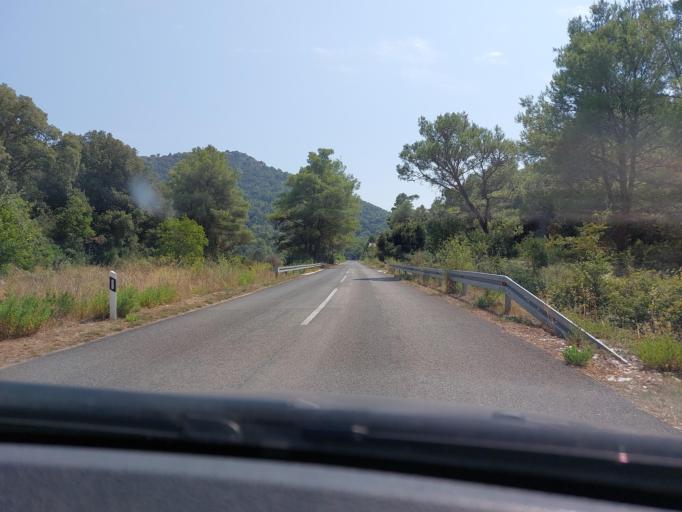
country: HR
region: Dubrovacko-Neretvanska
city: Smokvica
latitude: 42.7519
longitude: 16.8360
